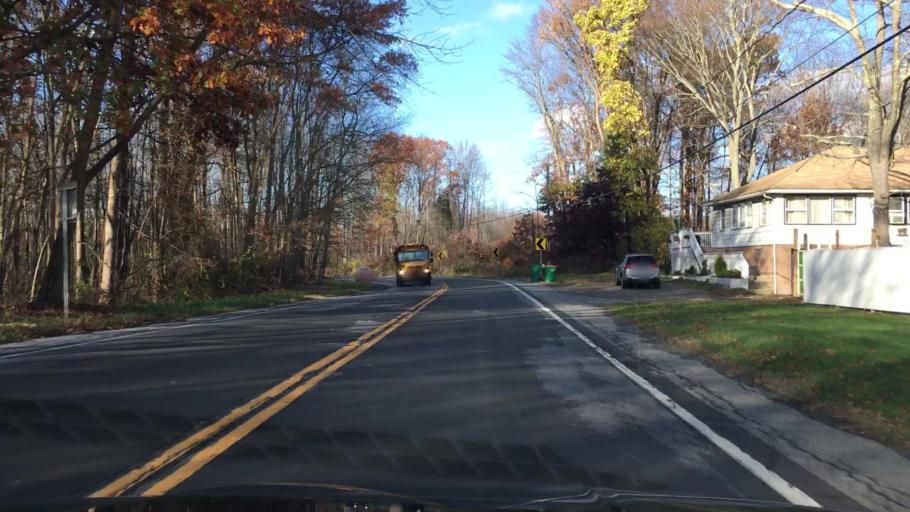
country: US
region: New York
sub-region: Dutchess County
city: Myers Corner
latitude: 41.6166
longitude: -73.8501
